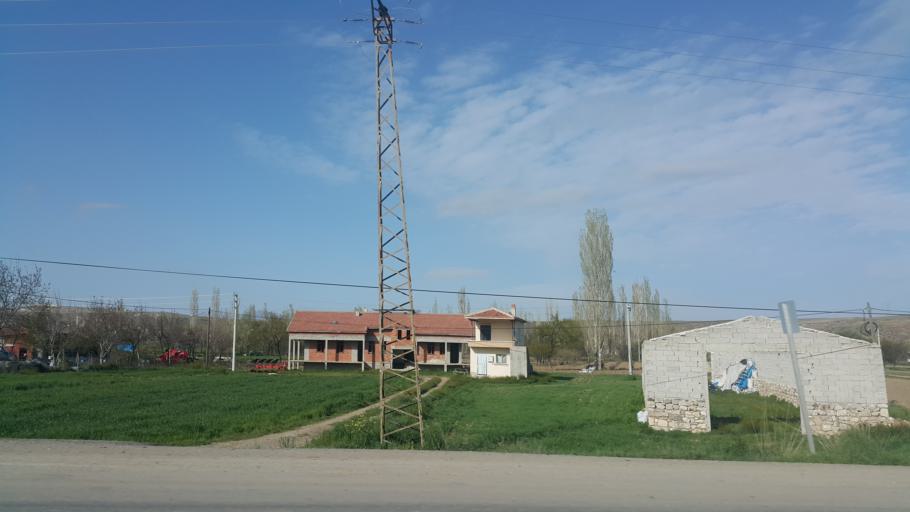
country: TR
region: Aksaray
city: Acipinar
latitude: 38.4737
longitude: 33.9005
